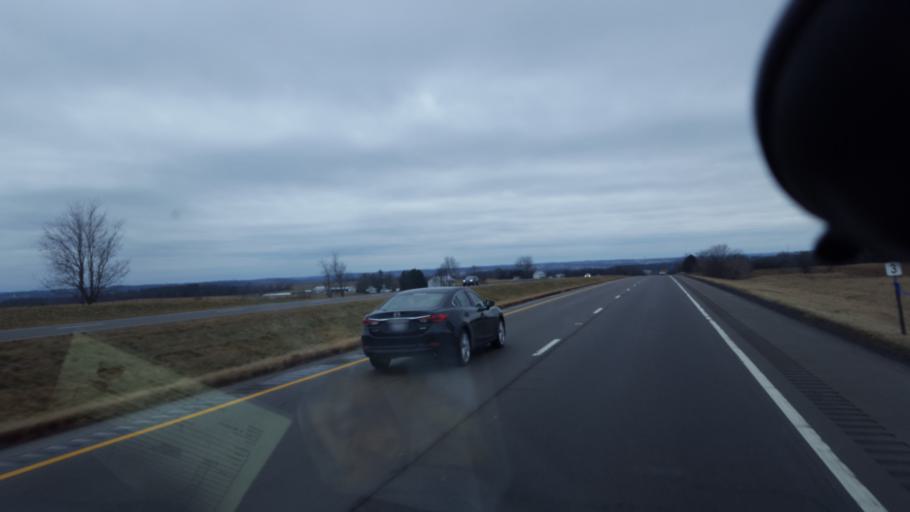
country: US
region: Ohio
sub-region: Wayne County
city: Shreve
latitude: 40.7908
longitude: -82.0707
